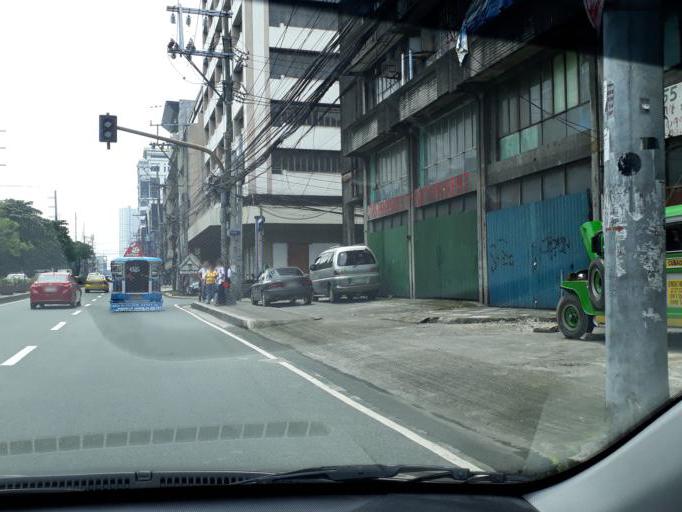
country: PH
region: Calabarzon
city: Del Monte
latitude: 14.6187
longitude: 121.0128
